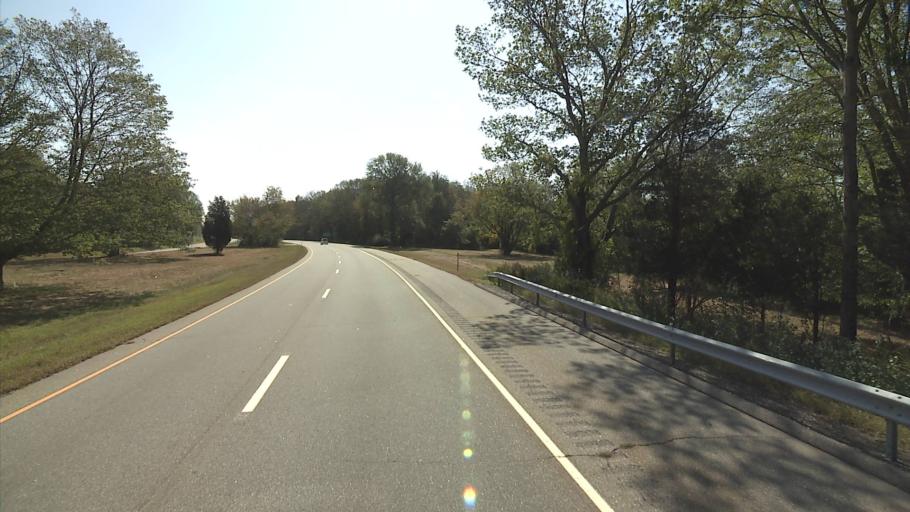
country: US
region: Connecticut
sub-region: New London County
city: Uncasville
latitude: 41.4262
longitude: -72.1225
